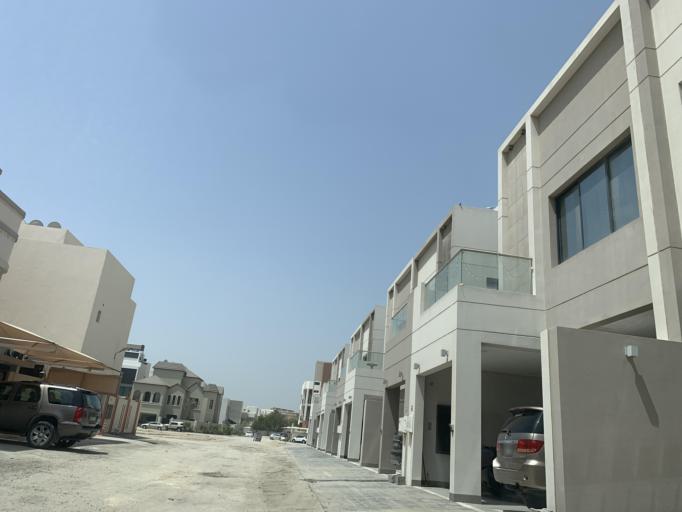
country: BH
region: Manama
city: Jidd Hafs
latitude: 26.1987
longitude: 50.5636
